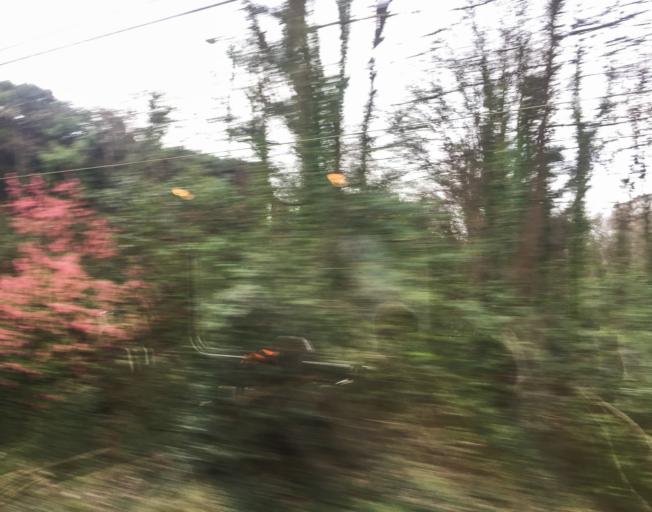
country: GB
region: Scotland
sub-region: West Dunbartonshire
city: Duntocher
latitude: 55.9142
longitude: -4.4327
